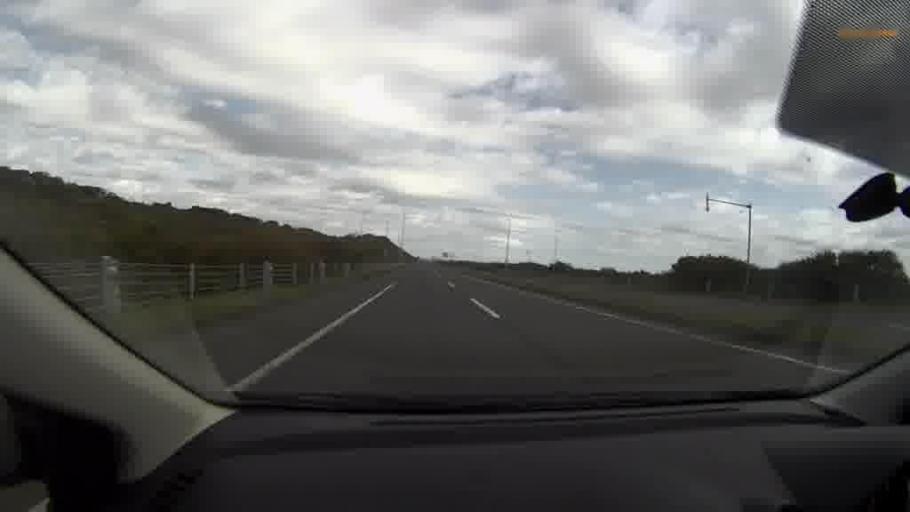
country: JP
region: Hokkaido
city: Kushiro
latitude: 43.0106
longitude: 144.2565
